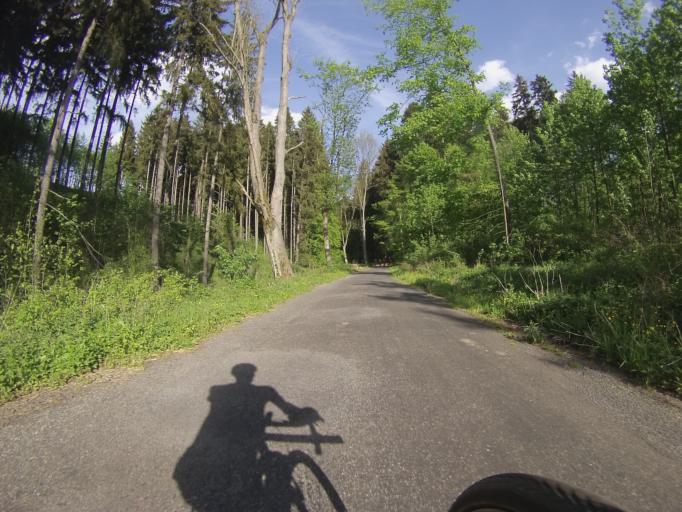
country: CZ
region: South Moravian
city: Ostrov u Macochy
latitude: 49.4007
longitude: 16.7350
